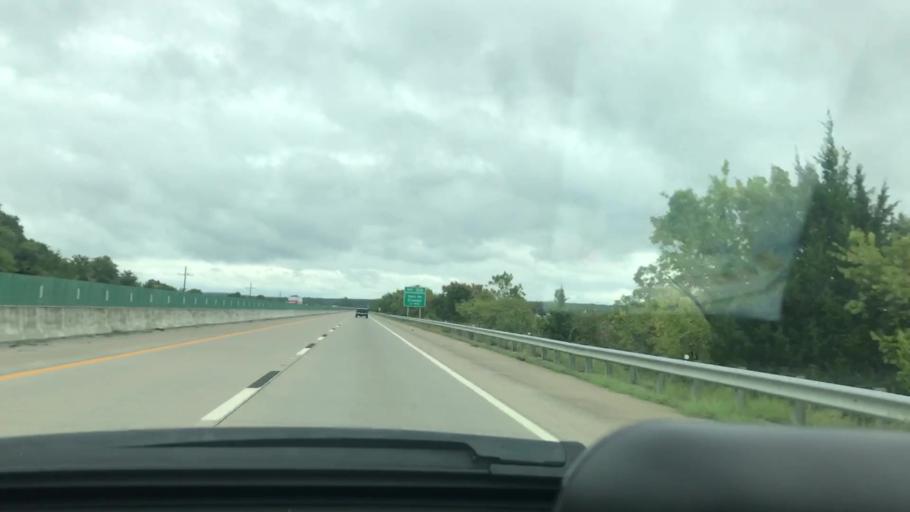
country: US
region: Oklahoma
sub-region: McIntosh County
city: Eufaula
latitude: 35.1217
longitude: -95.6813
